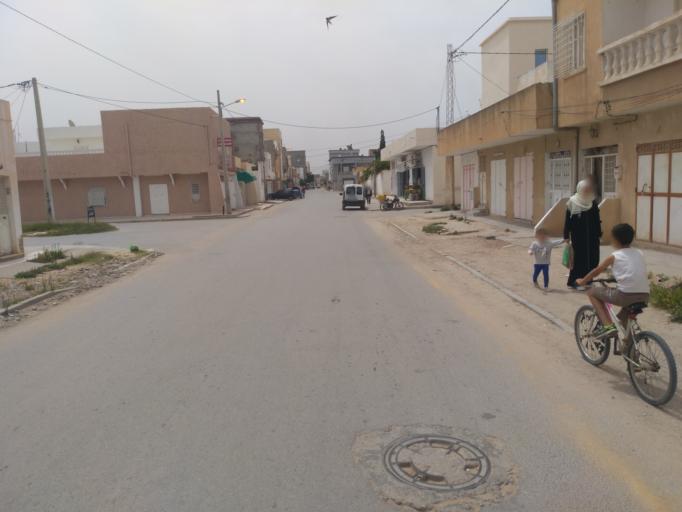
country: TN
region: Al Qayrawan
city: Kairouan
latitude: 35.6693
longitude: 10.0825
